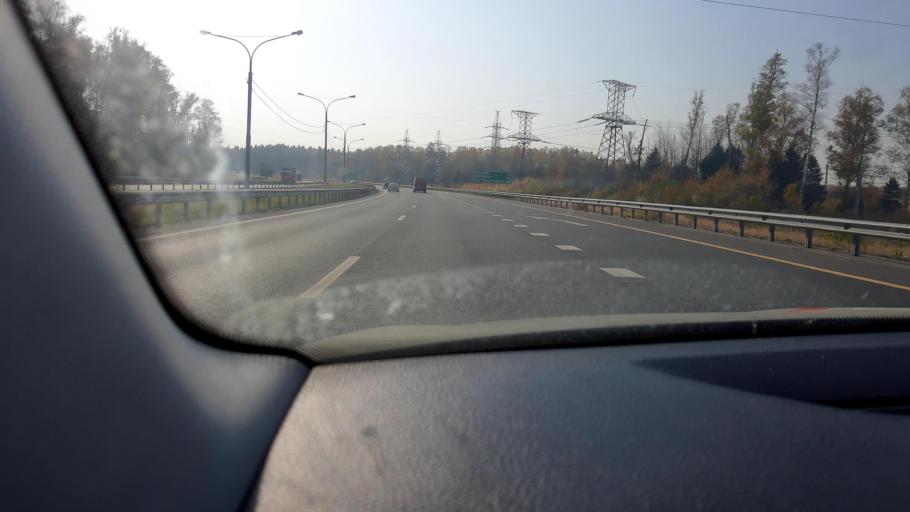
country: RU
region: Moskovskaya
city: Mikhnevo
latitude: 55.0726
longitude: 37.9332
